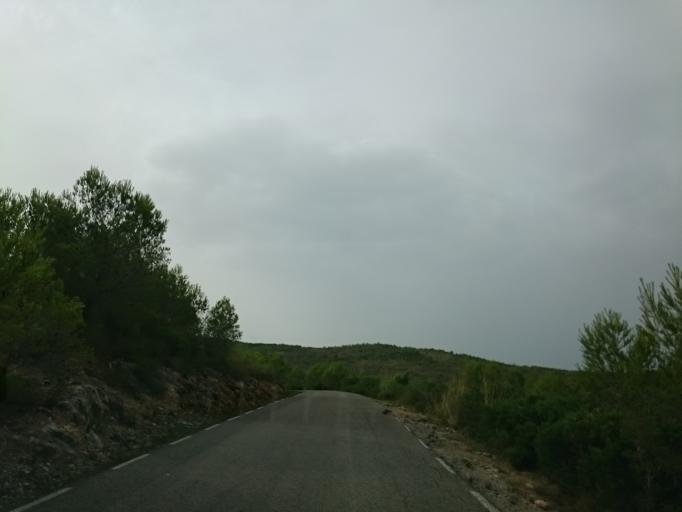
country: ES
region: Catalonia
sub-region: Provincia de Barcelona
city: Olivella
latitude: 41.3048
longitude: 1.8229
